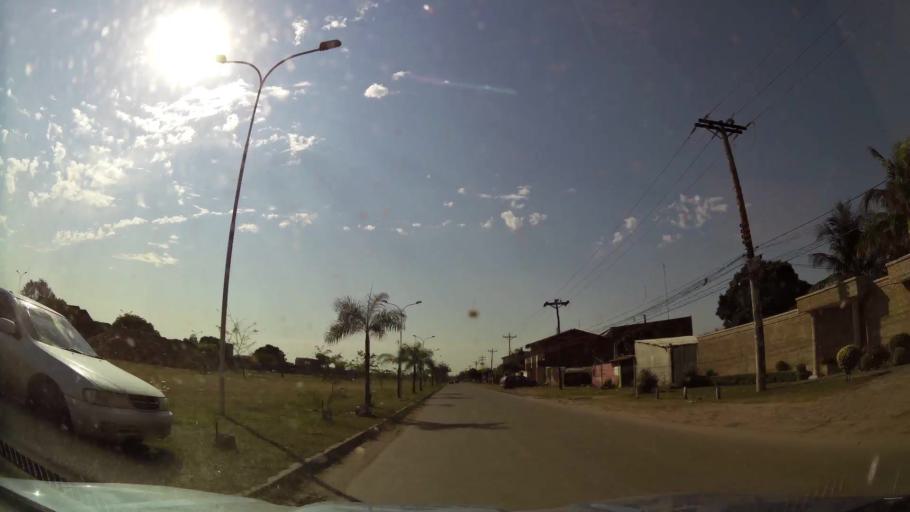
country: BO
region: Santa Cruz
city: Santa Cruz de la Sierra
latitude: -17.7999
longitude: -63.1420
